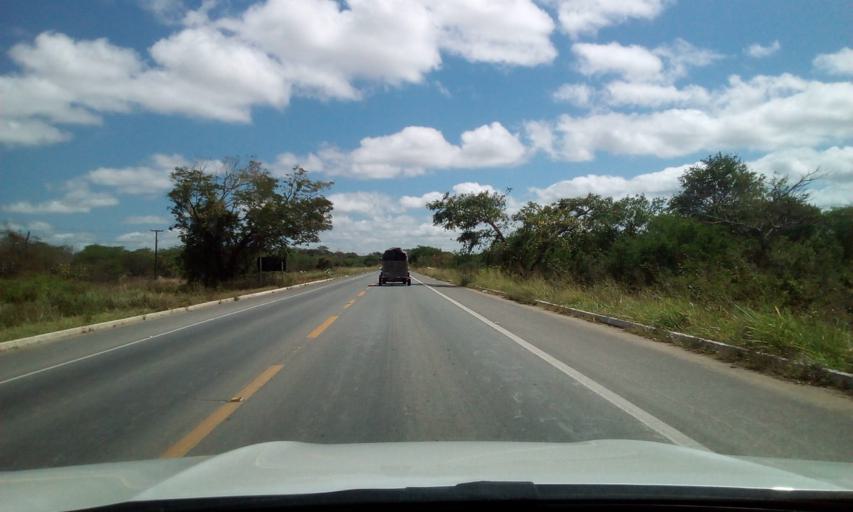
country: BR
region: Paraiba
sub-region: Campina Grande
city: Campina Grande
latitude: -7.3233
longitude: -35.8962
